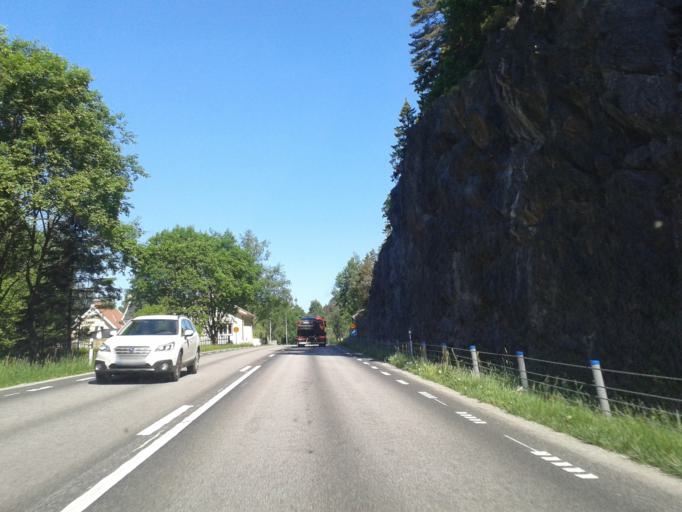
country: SE
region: Vaestra Goetaland
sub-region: Orust
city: Henan
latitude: 58.2261
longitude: 11.6856
